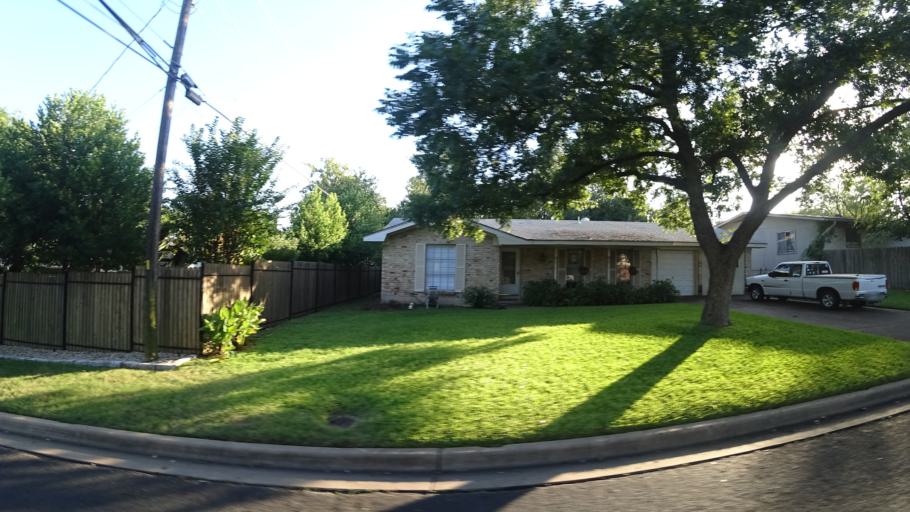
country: US
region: Texas
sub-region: Travis County
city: Wells Branch
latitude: 30.3598
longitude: -97.7025
